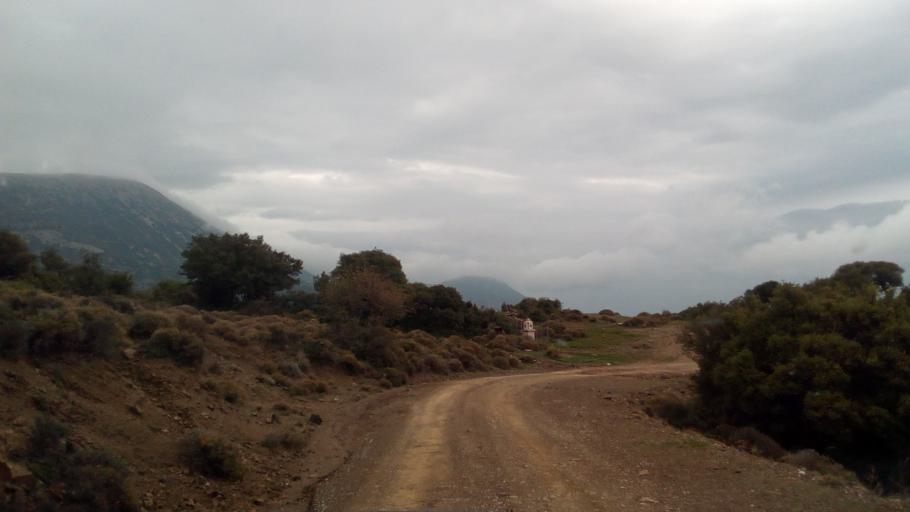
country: GR
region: West Greece
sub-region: Nomos Achaias
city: Selianitika
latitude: 38.4071
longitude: 22.0894
